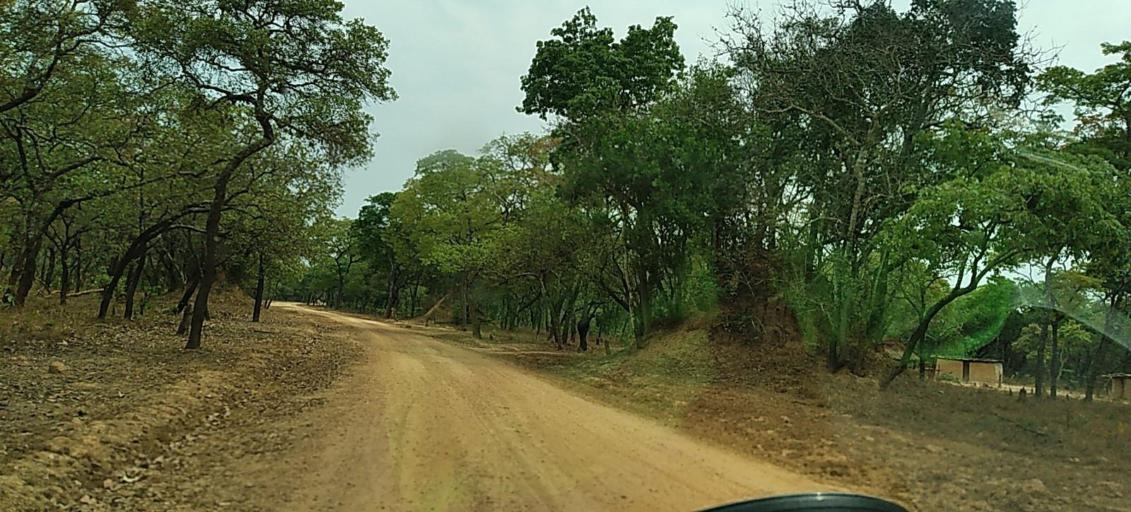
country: ZM
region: North-Western
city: Solwezi
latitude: -12.9291
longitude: 26.5606
